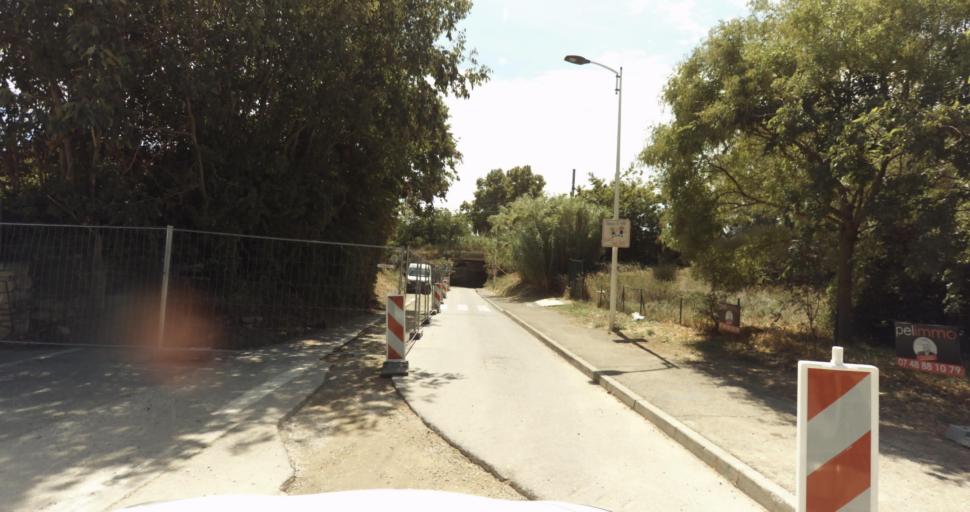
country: FR
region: Provence-Alpes-Cote d'Azur
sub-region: Departement des Bouches-du-Rhone
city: Miramas
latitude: 43.5788
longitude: 5.0148
